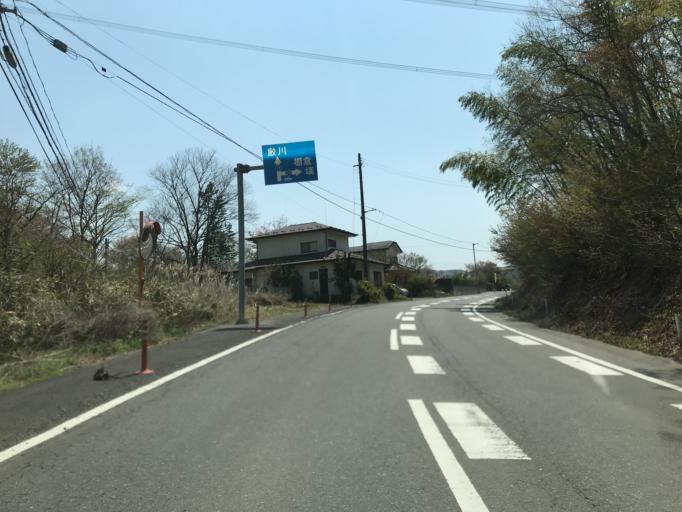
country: JP
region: Fukushima
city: Ishikawa
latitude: 37.0726
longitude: 140.4235
